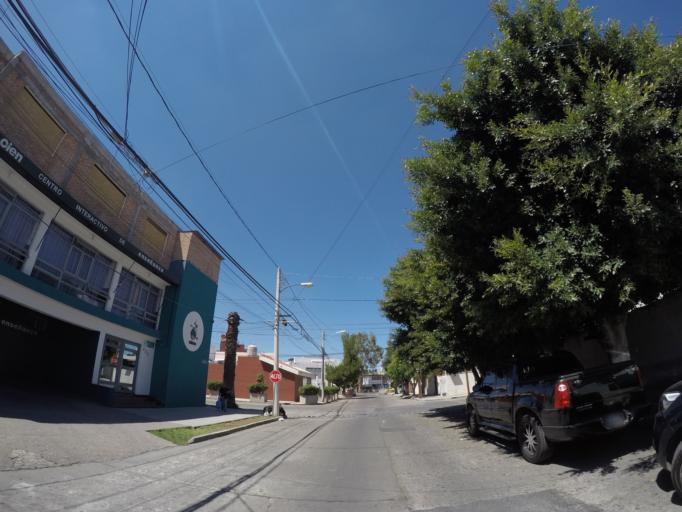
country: MX
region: San Luis Potosi
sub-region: San Luis Potosi
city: San Luis Potosi
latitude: 22.1471
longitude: -101.0075
